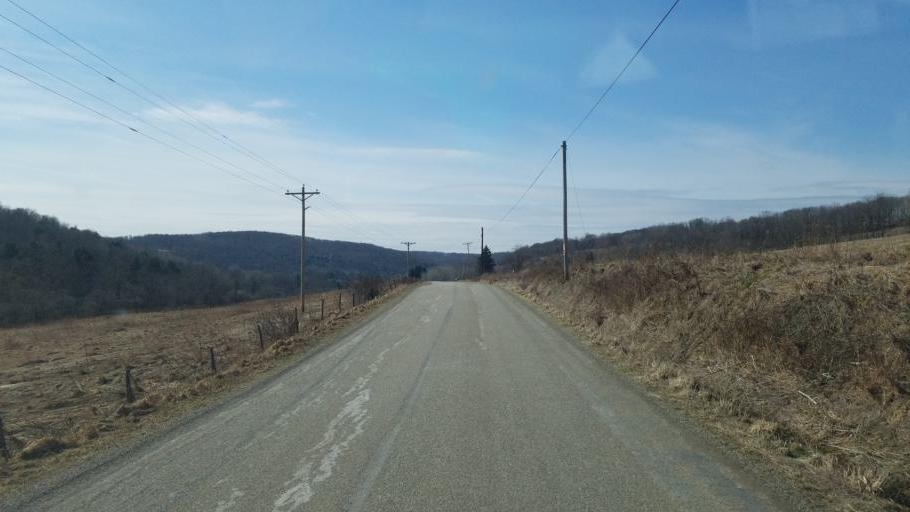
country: US
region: New York
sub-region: Allegany County
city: Andover
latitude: 41.9491
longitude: -77.8009
